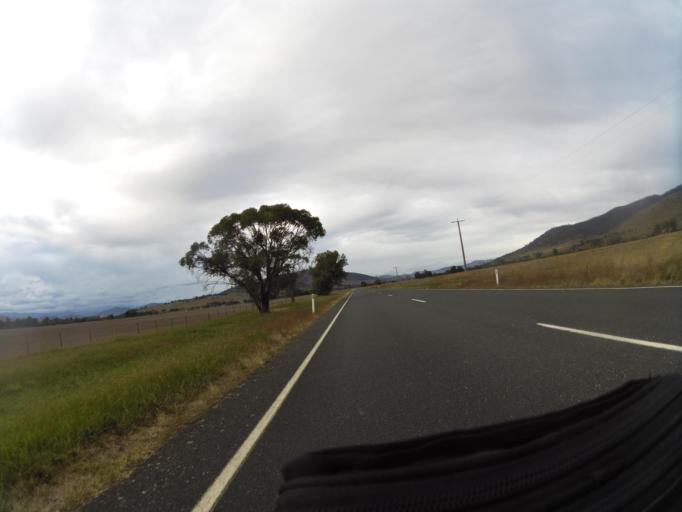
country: AU
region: New South Wales
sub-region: Snowy River
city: Jindabyne
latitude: -36.1049
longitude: 147.9803
